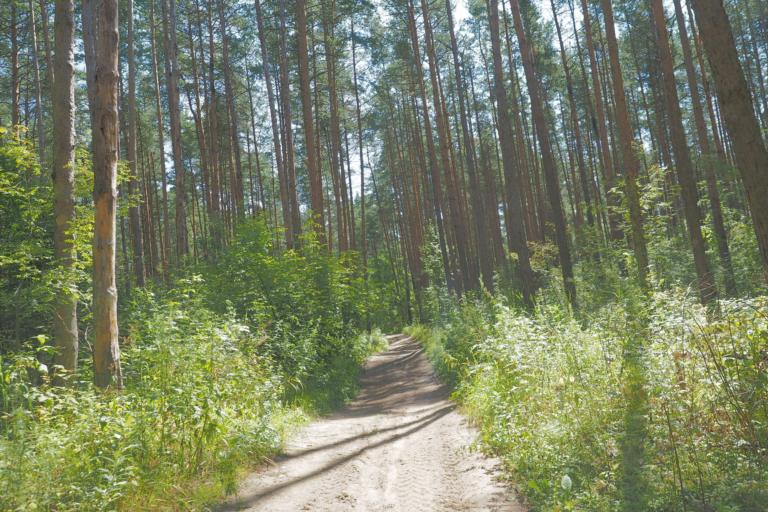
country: RU
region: Moskovskaya
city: Malyshevo
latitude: 55.5283
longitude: 38.3444
